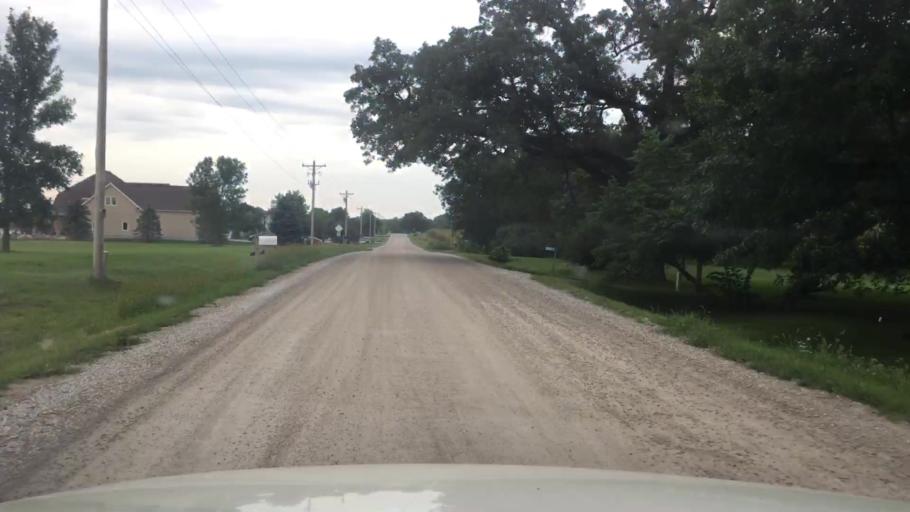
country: US
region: Iowa
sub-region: Story County
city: Huxley
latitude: 41.9174
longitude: -93.5766
